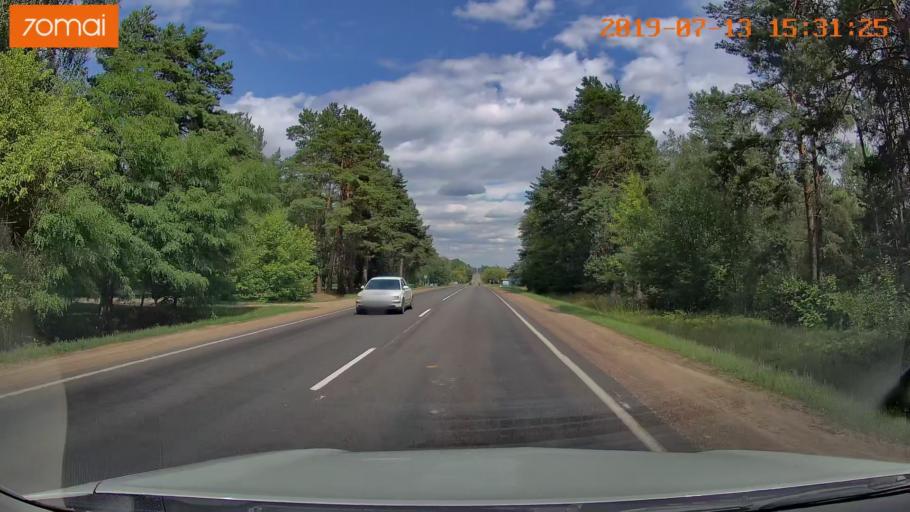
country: BY
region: Mogilev
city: Babruysk
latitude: 53.1134
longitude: 29.1053
